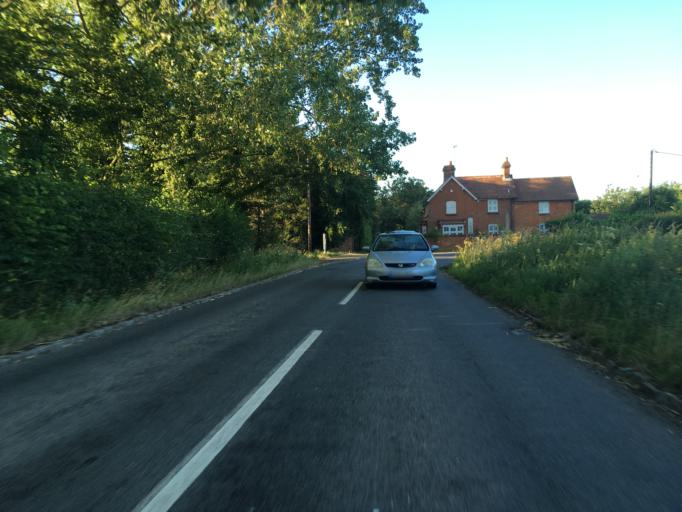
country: GB
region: England
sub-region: Hampshire
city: Tadley
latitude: 51.4127
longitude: -1.1370
